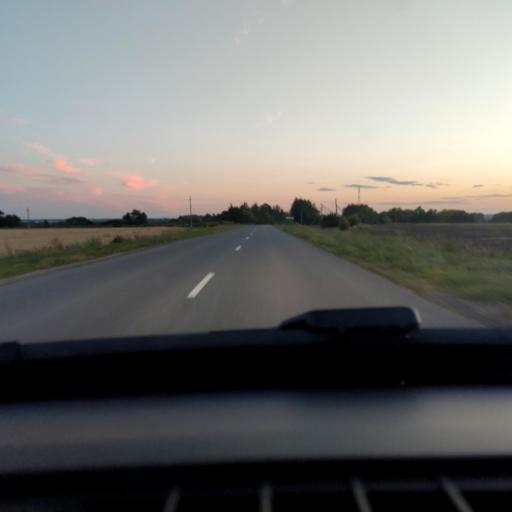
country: RU
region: Lipetsk
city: Zadonsk
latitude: 52.2967
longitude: 38.7874
